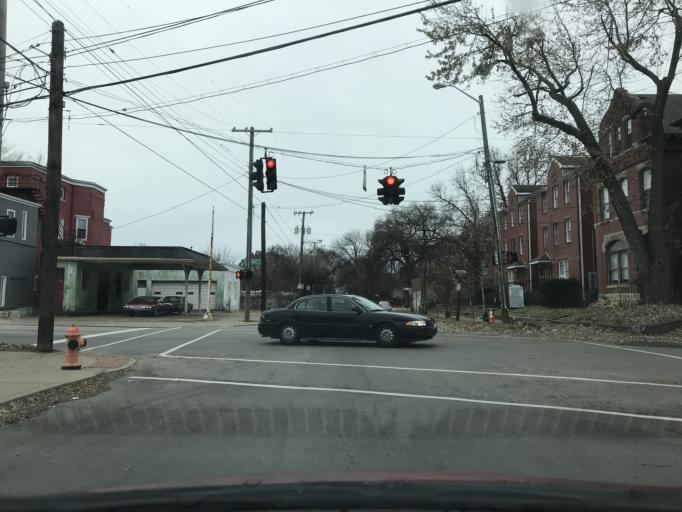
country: US
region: Kentucky
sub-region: Jefferson County
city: Louisville
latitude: 38.2425
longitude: -85.7624
